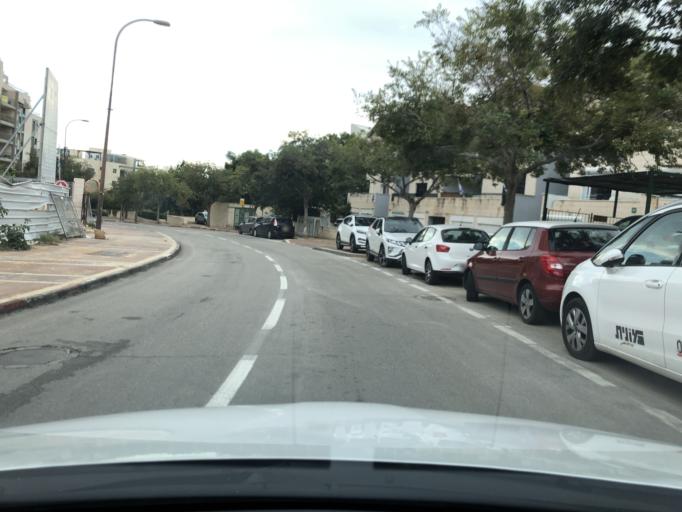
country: IL
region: Central District
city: Modiin
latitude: 31.9073
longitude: 35.0102
